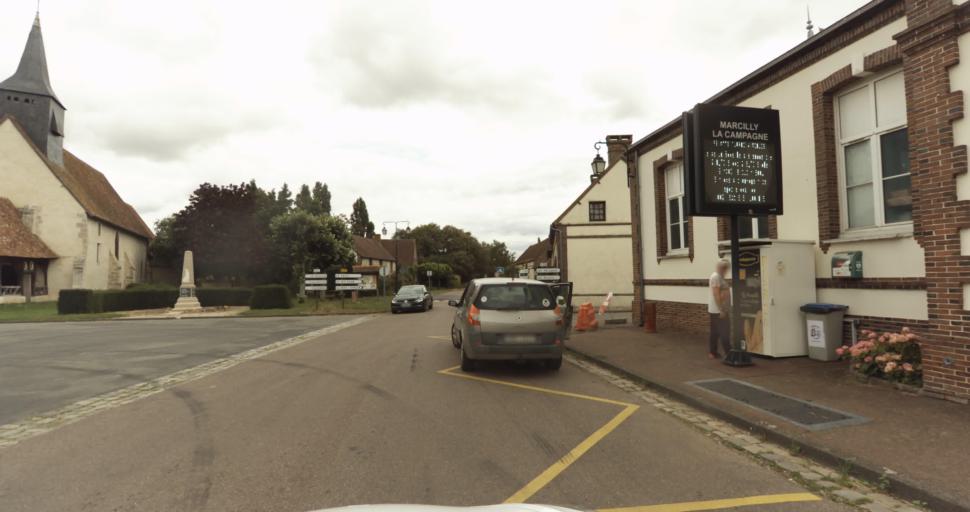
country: FR
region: Haute-Normandie
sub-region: Departement de l'Eure
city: La Madeleine-de-Nonancourt
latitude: 48.8336
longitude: 1.2011
